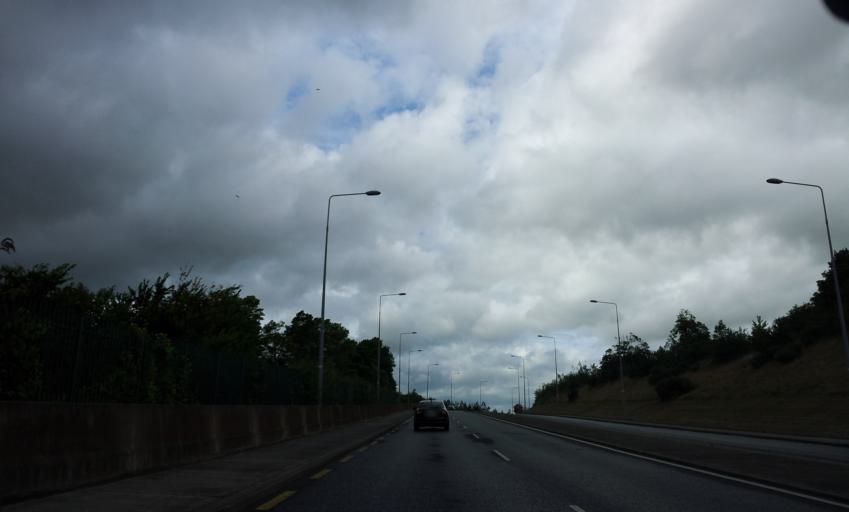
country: IE
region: Munster
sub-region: Waterford
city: Waterford
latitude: 52.2693
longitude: -7.1309
